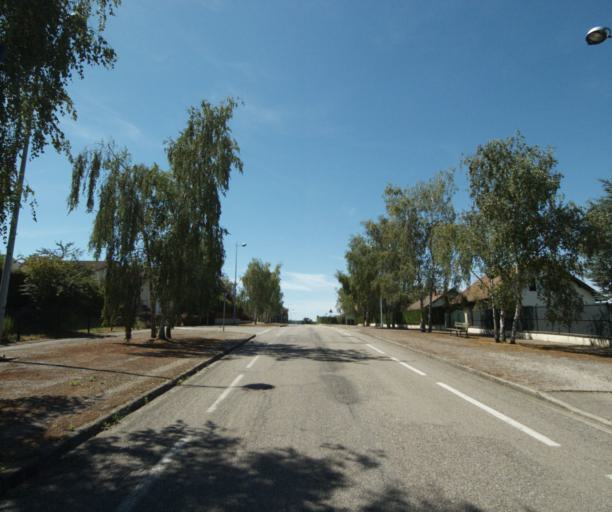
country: FR
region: Lorraine
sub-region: Departement des Vosges
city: Epinal
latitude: 48.1910
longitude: 6.4537
